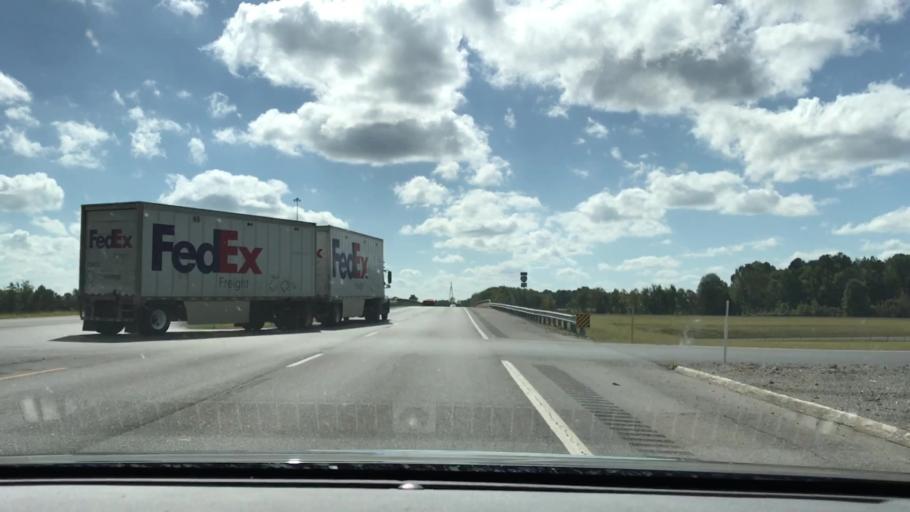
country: US
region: Kentucky
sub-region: McCracken County
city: Reidland
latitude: 36.9961
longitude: -88.5062
